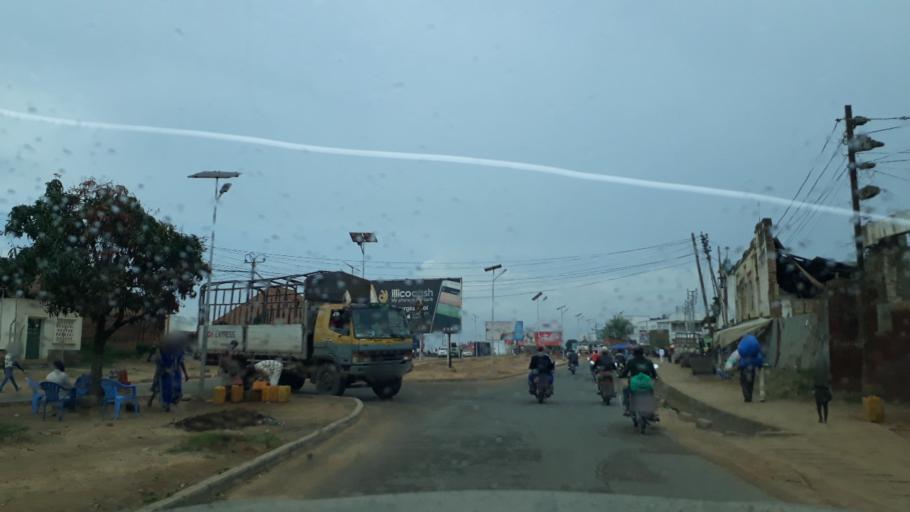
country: CD
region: Eastern Province
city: Bunia
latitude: 1.5611
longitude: 30.2480
